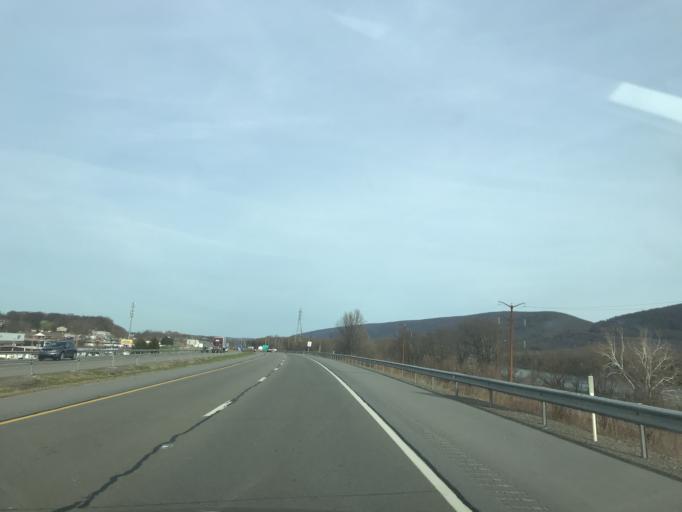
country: US
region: Pennsylvania
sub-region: Lycoming County
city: Faxon
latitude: 41.2469
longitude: -76.9699
